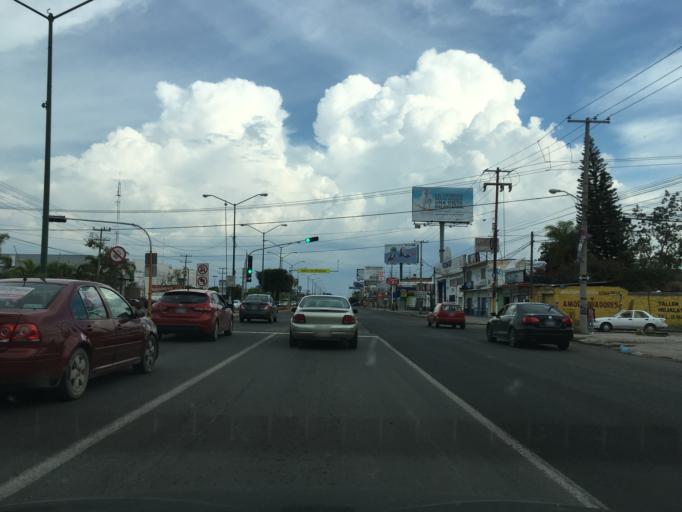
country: MX
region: Guanajuato
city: Celaya
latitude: 20.5478
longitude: -100.8219
